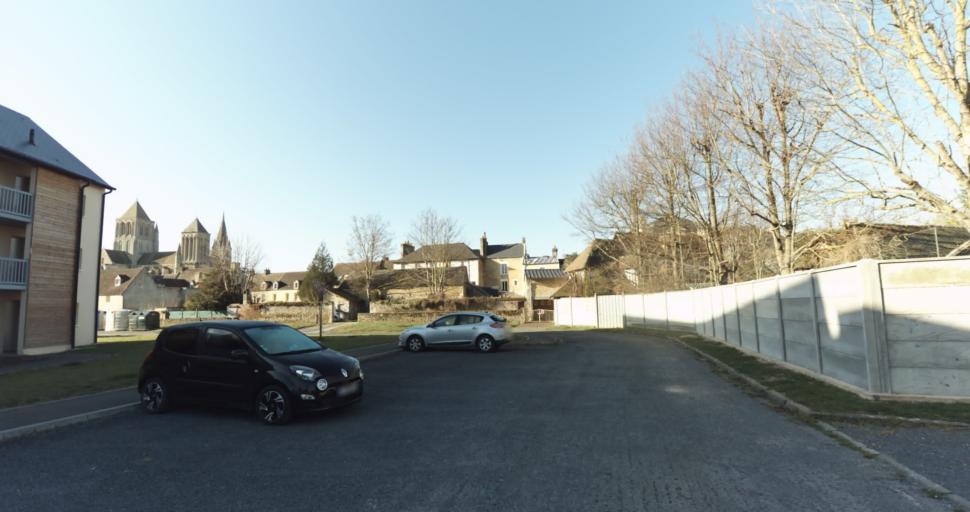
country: FR
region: Lower Normandy
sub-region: Departement du Calvados
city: Saint-Pierre-sur-Dives
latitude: 49.0222
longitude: -0.0335
